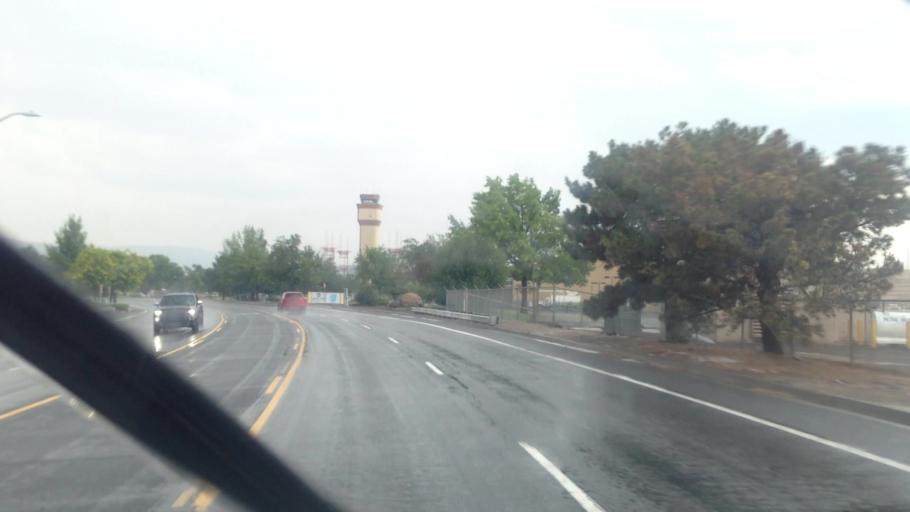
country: US
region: Nevada
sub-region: Washoe County
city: Sparks
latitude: 39.5044
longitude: -119.7641
